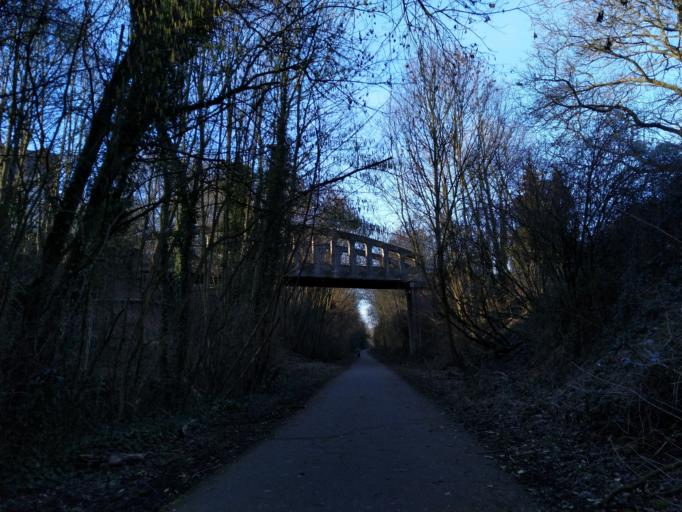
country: BE
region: Wallonia
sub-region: Province du Hainaut
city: Frameries
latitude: 50.4102
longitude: 3.9052
